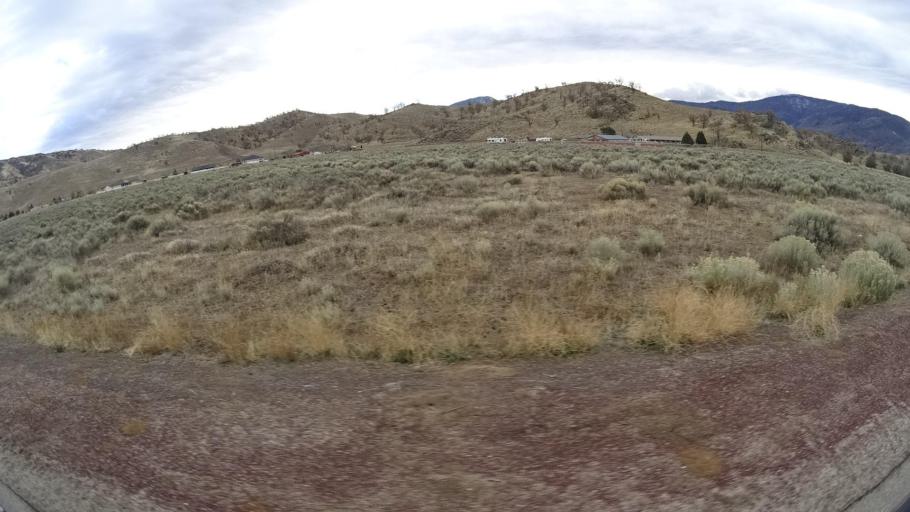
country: US
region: California
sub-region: Kern County
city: Bear Valley Springs
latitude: 35.1257
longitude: -118.5735
